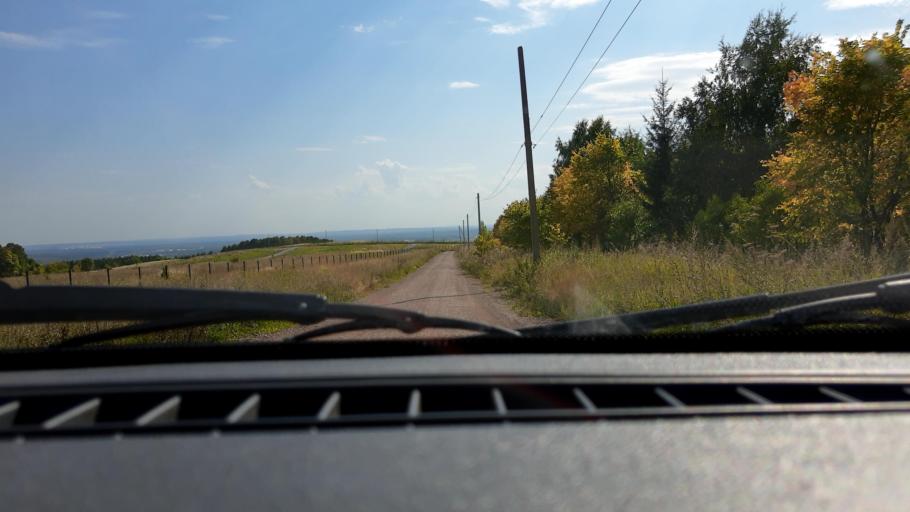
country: RU
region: Bashkortostan
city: Ufa
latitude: 54.8532
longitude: 56.1634
